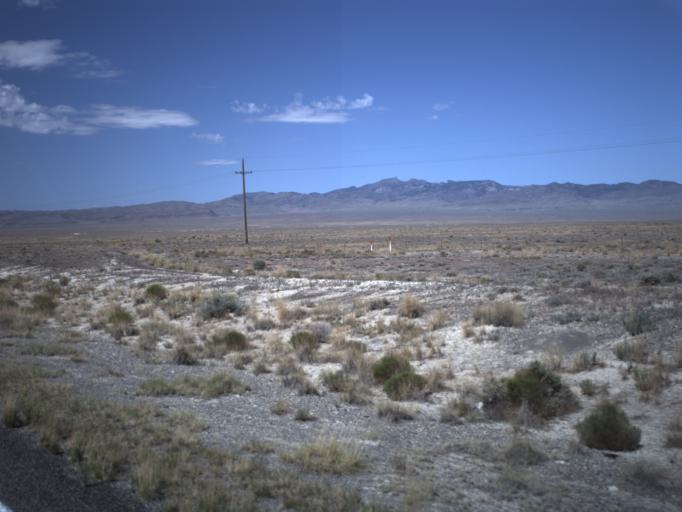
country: US
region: Utah
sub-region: Millard County
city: Delta
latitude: 39.1273
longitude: -113.1085
